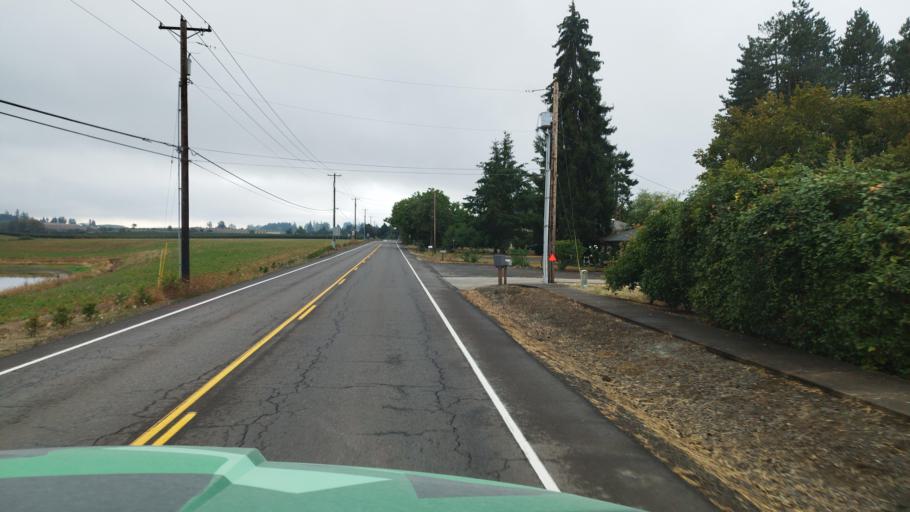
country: US
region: Oregon
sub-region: Yamhill County
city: Yamhill
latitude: 45.3364
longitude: -123.1863
